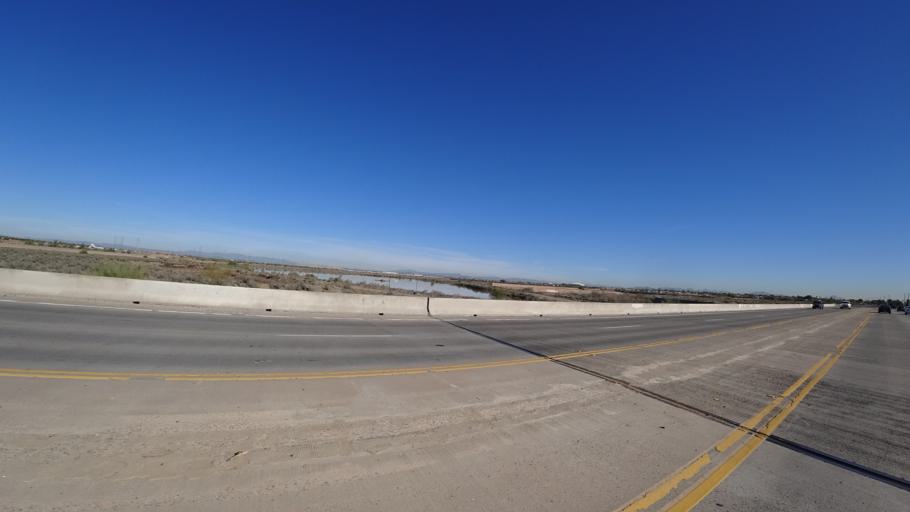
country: US
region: Arizona
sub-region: Maricopa County
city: Litchfield Park
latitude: 33.4931
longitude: -112.3144
